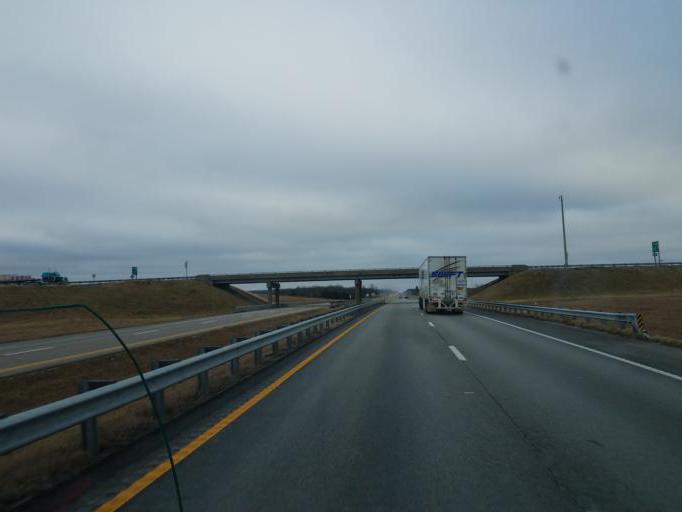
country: US
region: Missouri
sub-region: Webster County
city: Marshfield
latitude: 37.5052
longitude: -92.8414
